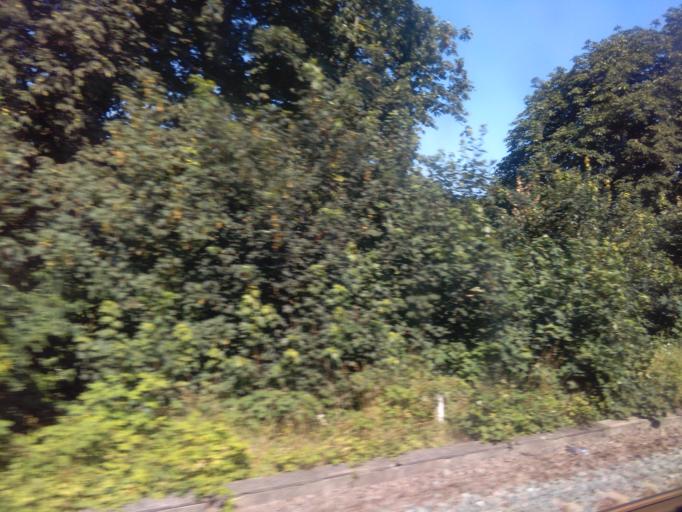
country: GB
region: England
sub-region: Luton
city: Luton
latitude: 51.8844
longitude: -0.4226
